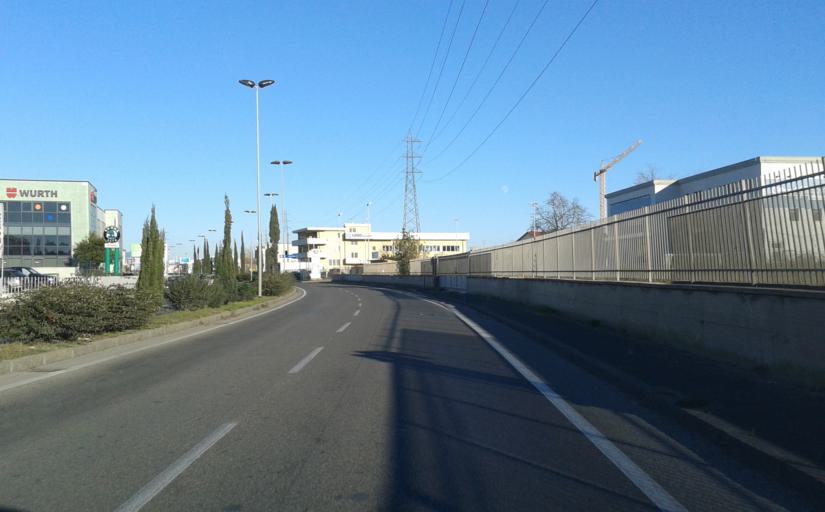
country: IT
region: Tuscany
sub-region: Provincia di Livorno
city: Livorno
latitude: 43.5726
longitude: 10.3317
